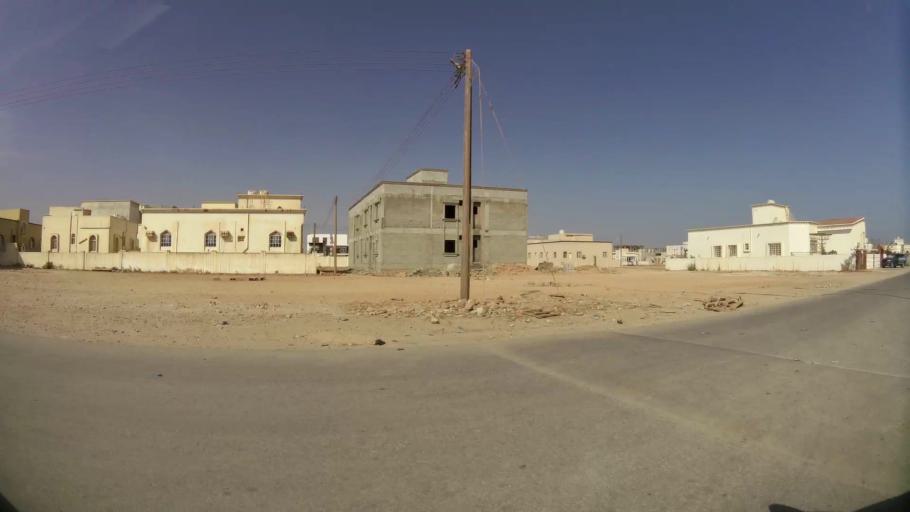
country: OM
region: Zufar
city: Salalah
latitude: 17.0082
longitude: 54.0036
